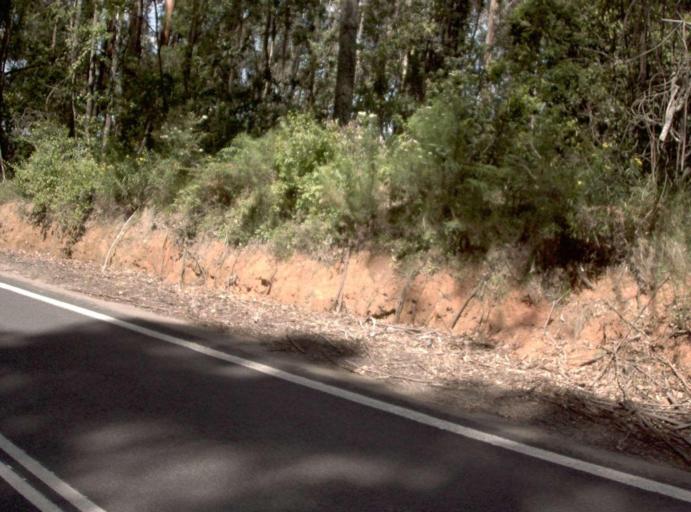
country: AU
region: New South Wales
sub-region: Bombala
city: Bombala
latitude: -37.5572
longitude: 149.3534
